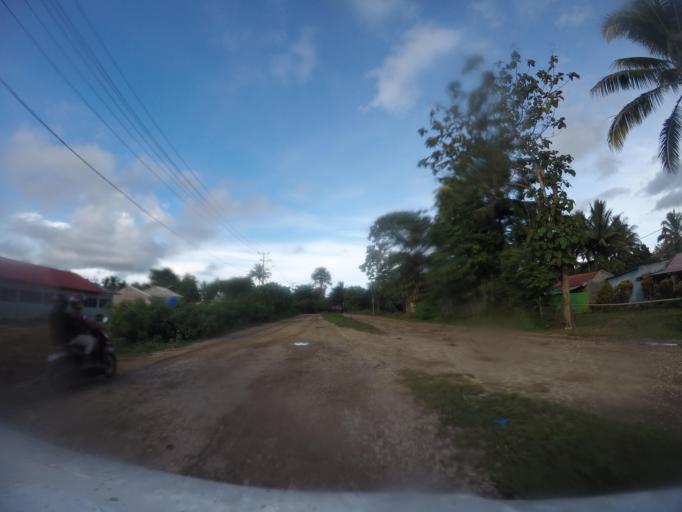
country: TL
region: Lautem
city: Lospalos
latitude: -8.5043
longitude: 127.0070
